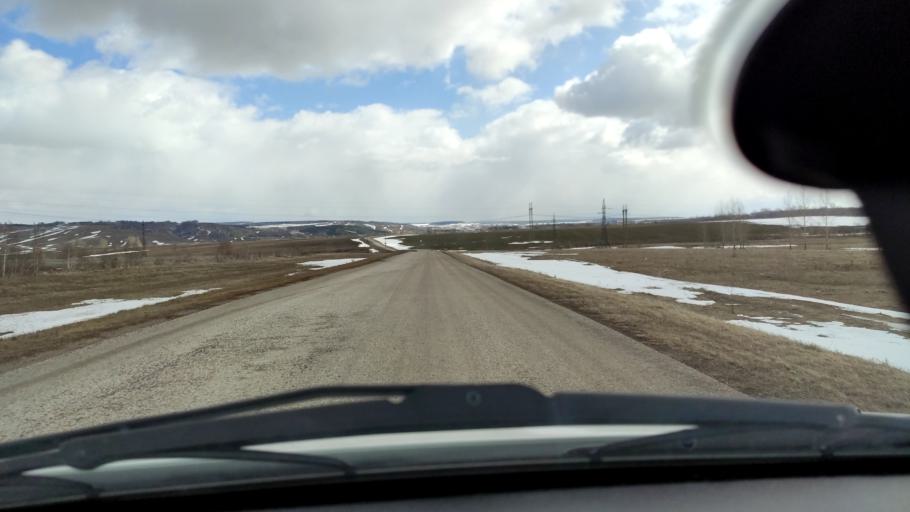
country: RU
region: Bashkortostan
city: Tolbazy
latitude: 54.1707
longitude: 55.9134
